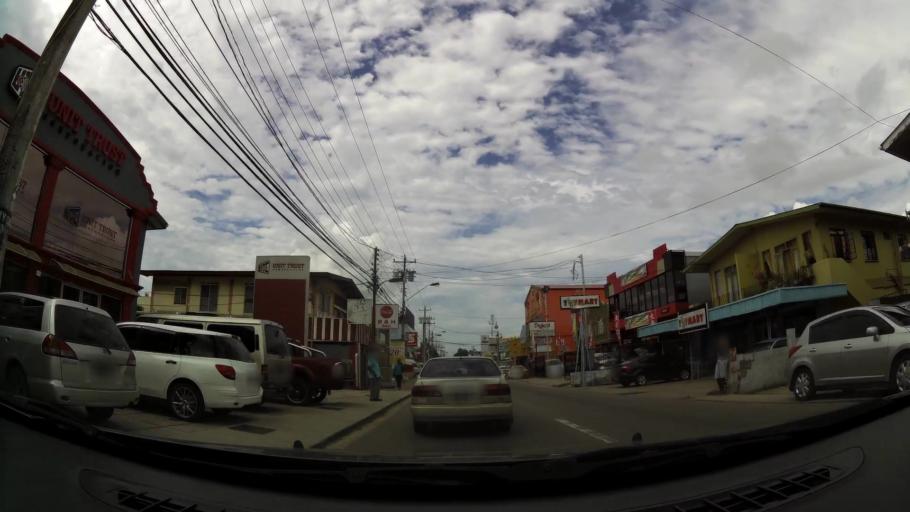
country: TT
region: Couva-Tabaquite-Talparo
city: Couva
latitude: 10.4217
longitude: -61.4568
